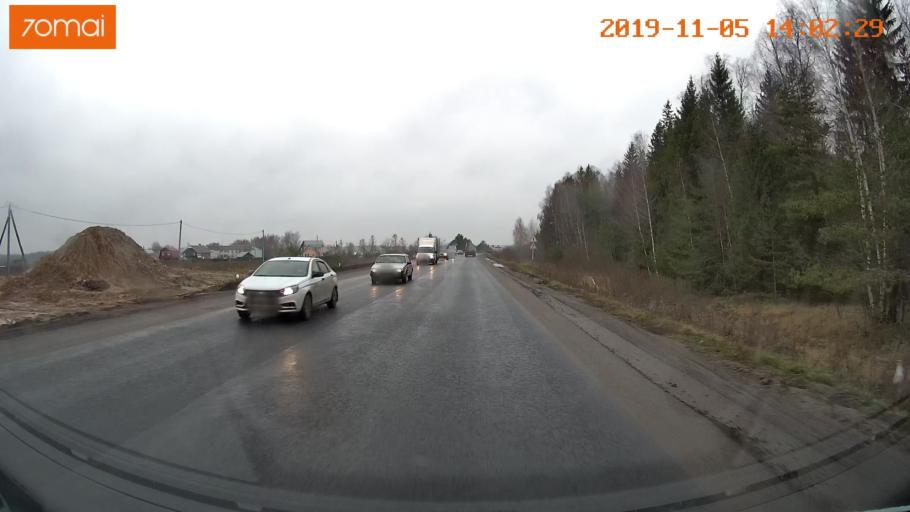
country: RU
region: Ivanovo
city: Kokhma
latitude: 57.0014
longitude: 41.2128
